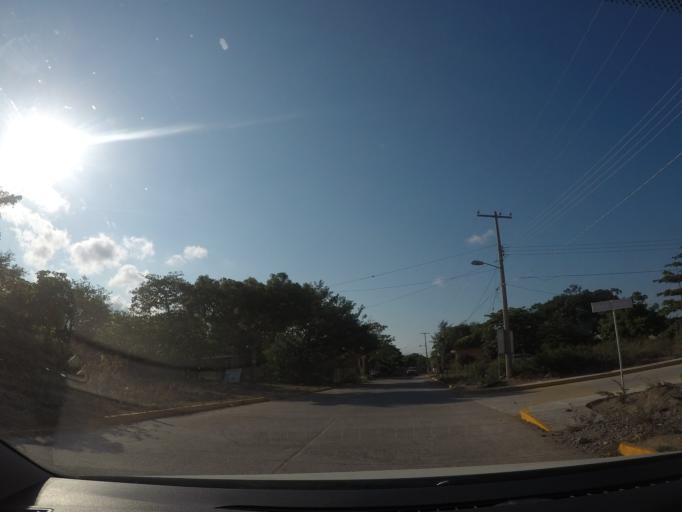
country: MX
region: Oaxaca
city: Juchitan de Zaragoza
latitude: 16.4198
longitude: -95.0229
